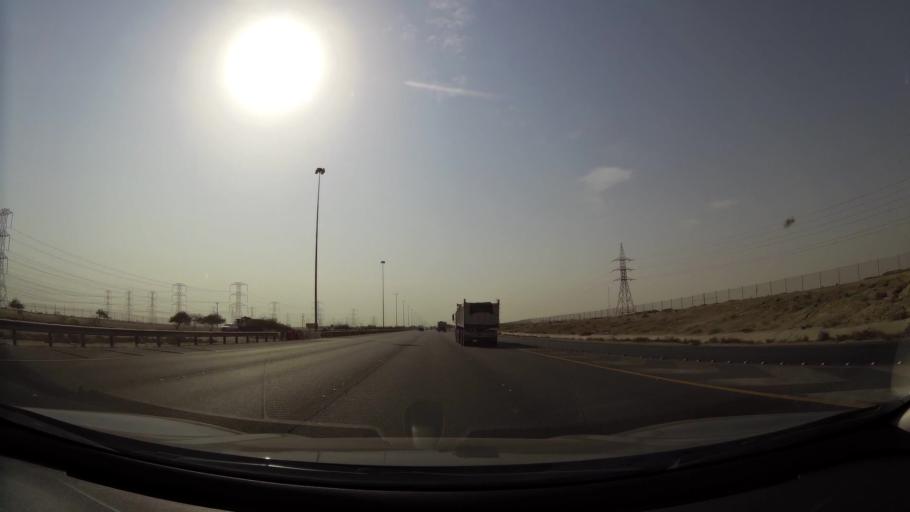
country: KW
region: Al Ahmadi
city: Al Ahmadi
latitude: 28.9878
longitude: 48.1036
